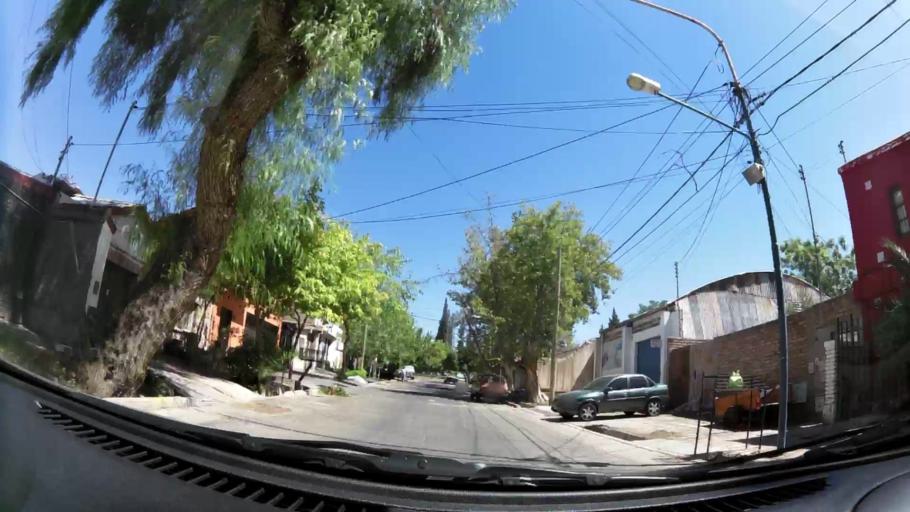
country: AR
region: Mendoza
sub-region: Departamento de Godoy Cruz
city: Godoy Cruz
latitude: -32.9098
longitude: -68.8636
